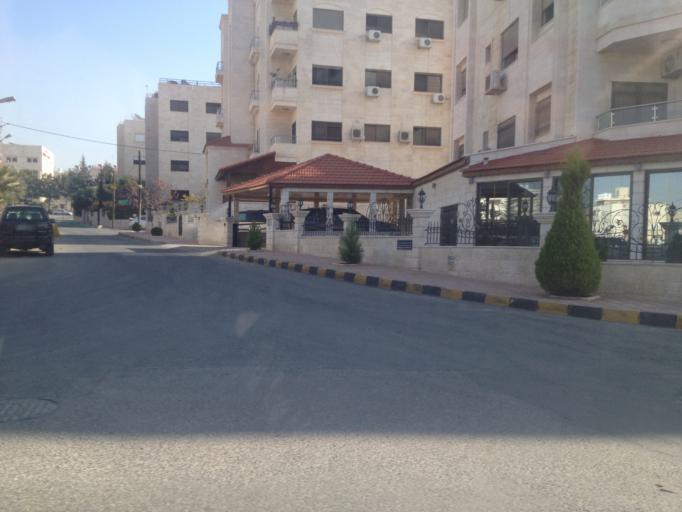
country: JO
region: Amman
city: Wadi as Sir
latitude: 31.9515
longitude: 35.8571
